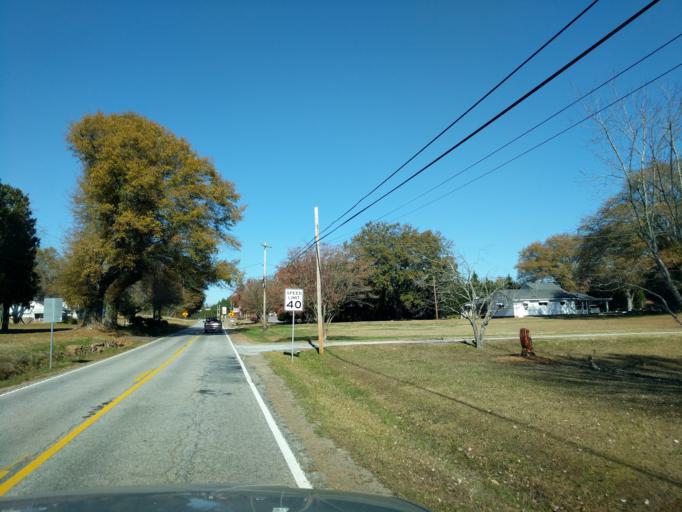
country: US
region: South Carolina
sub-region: Spartanburg County
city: Inman Mills
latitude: 35.0237
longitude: -82.1839
